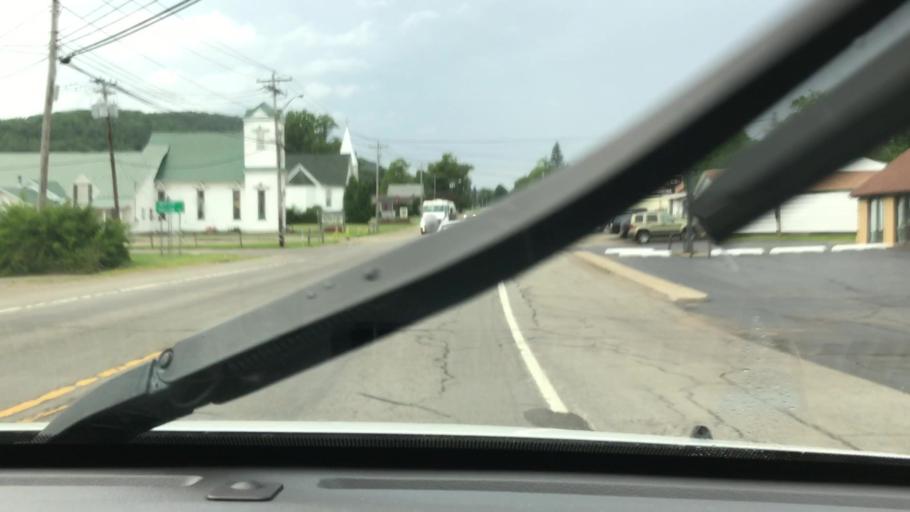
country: US
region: New York
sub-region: Cattaraugus County
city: Salamanca
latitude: 42.2152
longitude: -78.6370
